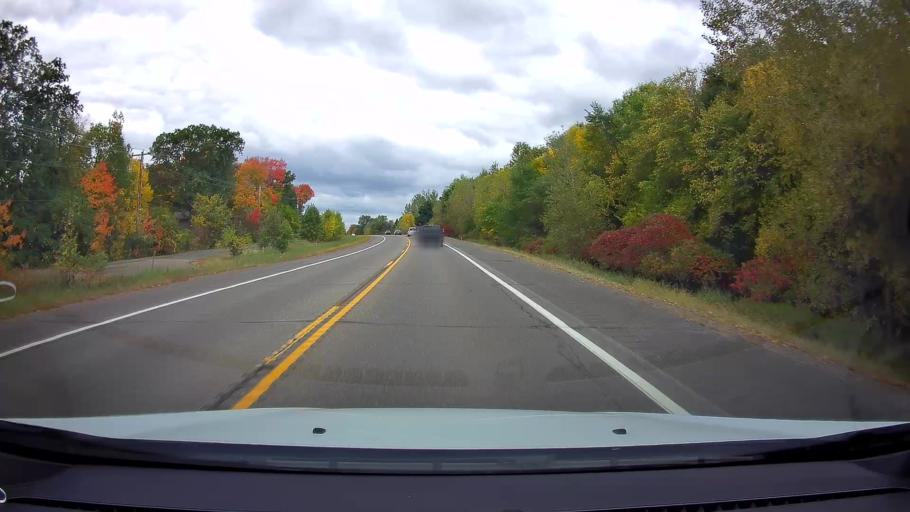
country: US
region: Minnesota
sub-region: Chisago County
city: Chisago City
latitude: 45.3638
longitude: -92.9056
